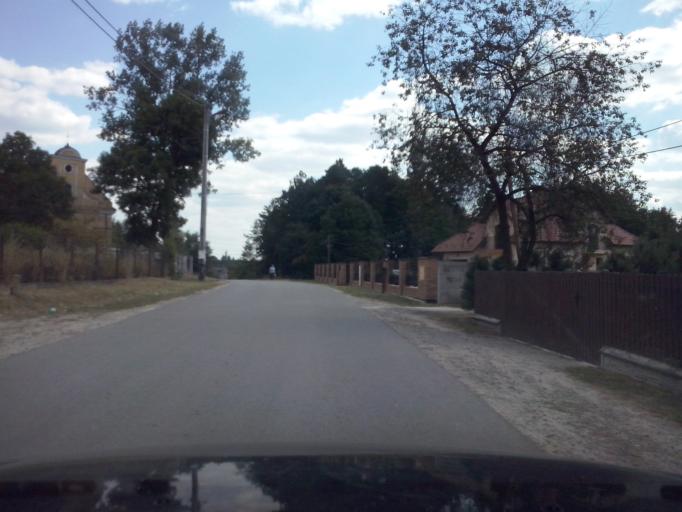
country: PL
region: Swietokrzyskie
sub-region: Powiat staszowski
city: Staszow
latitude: 50.5419
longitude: 21.1315
